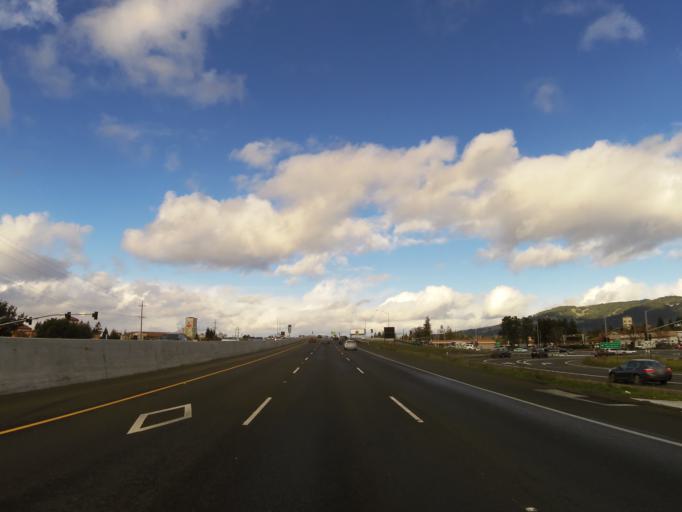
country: US
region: California
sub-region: Sonoma County
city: Rohnert Park
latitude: 38.3610
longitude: -122.7132
